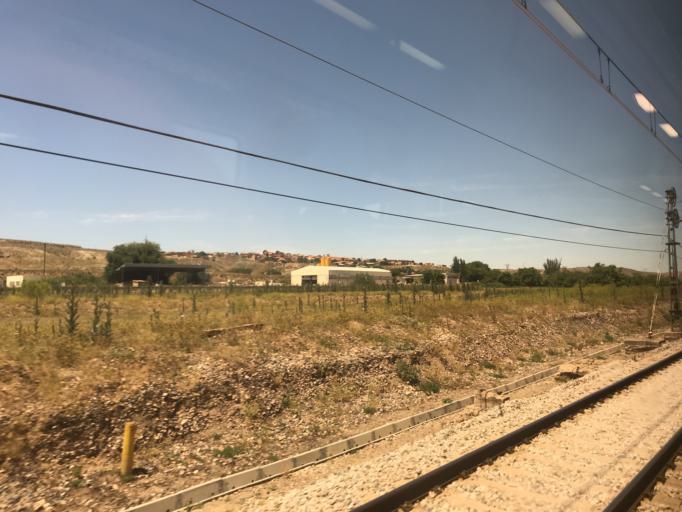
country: ES
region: Madrid
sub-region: Provincia de Madrid
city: Ciempozuelos
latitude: 40.0991
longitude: -3.6274
